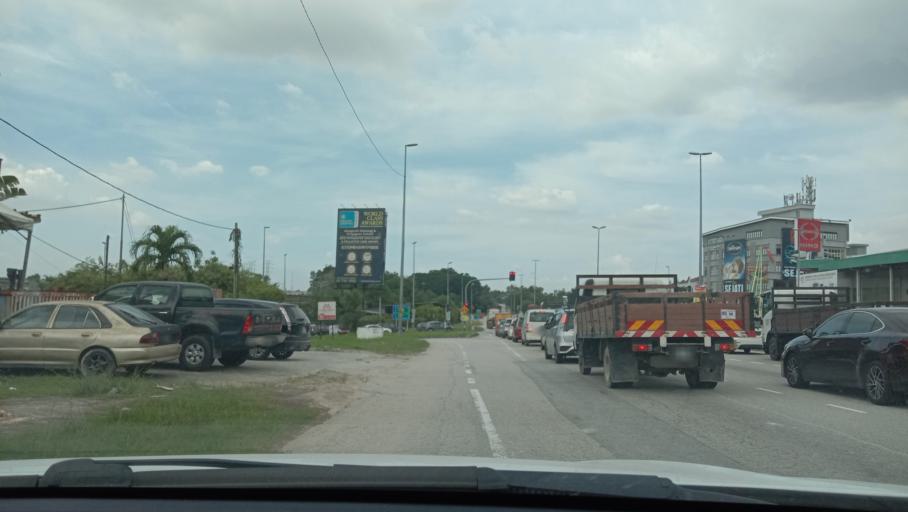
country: MY
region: Selangor
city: Kampung Baru Subang
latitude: 3.1369
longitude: 101.5257
